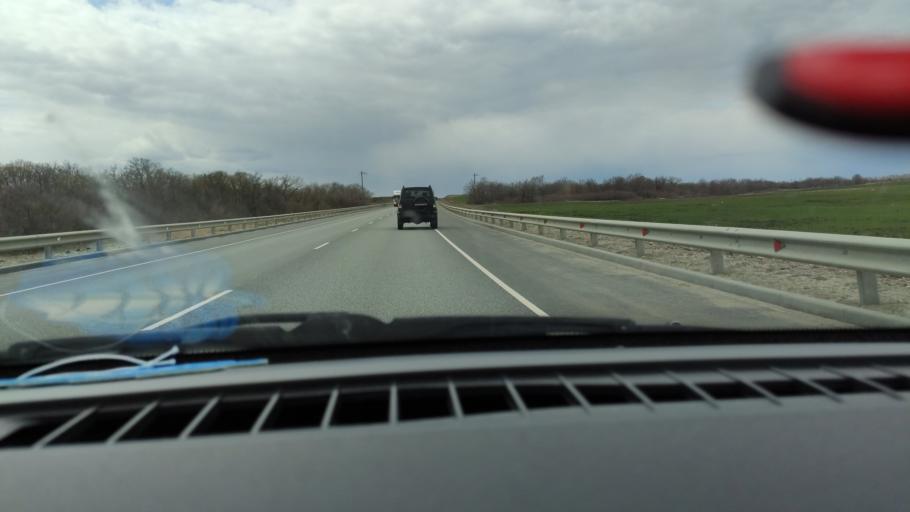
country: RU
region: Saratov
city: Yelshanka
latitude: 51.8306
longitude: 46.4416
